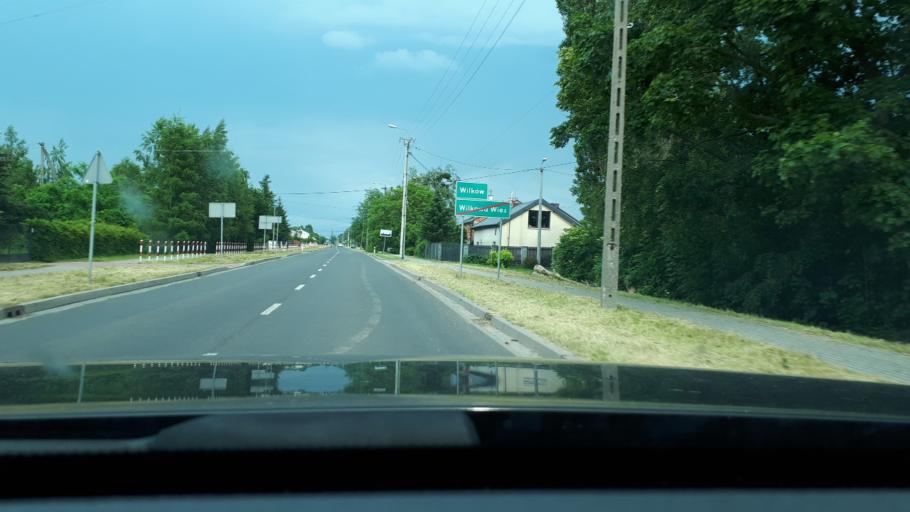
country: PL
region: Masovian Voivodeship
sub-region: Powiat warszawski zachodni
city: Leszno
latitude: 52.2580
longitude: 20.5475
